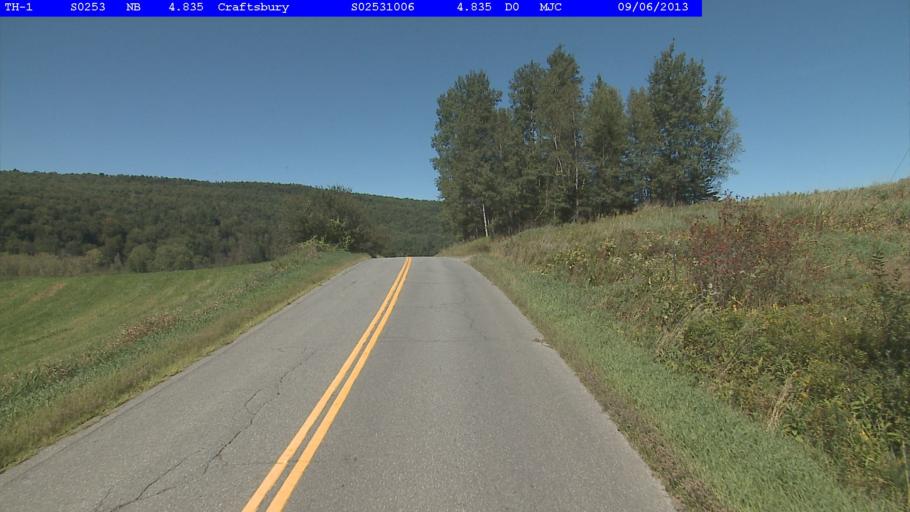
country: US
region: Vermont
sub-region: Caledonia County
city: Hardwick
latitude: 44.6742
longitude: -72.3951
